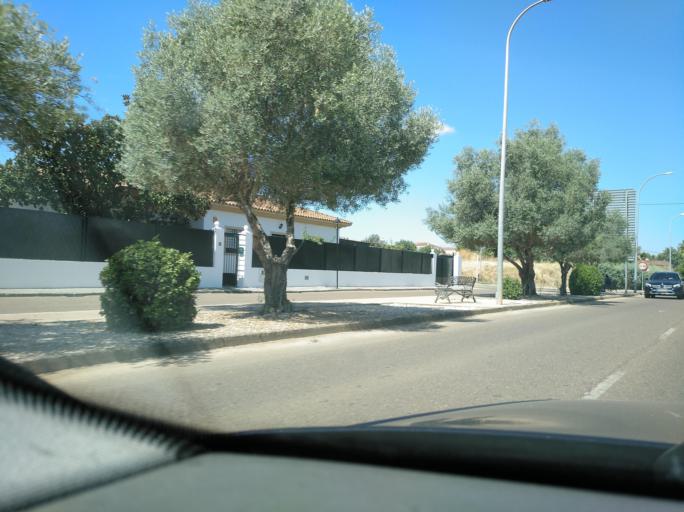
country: ES
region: Extremadura
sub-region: Provincia de Badajoz
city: Olivenza
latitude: 38.6886
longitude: -7.0964
